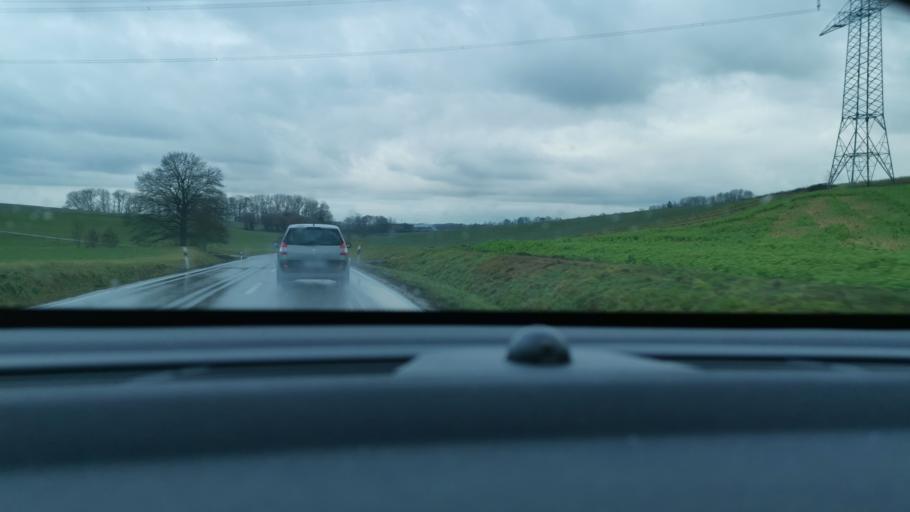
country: DE
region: Bavaria
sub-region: Swabia
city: Affing
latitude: 48.4699
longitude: 10.9918
